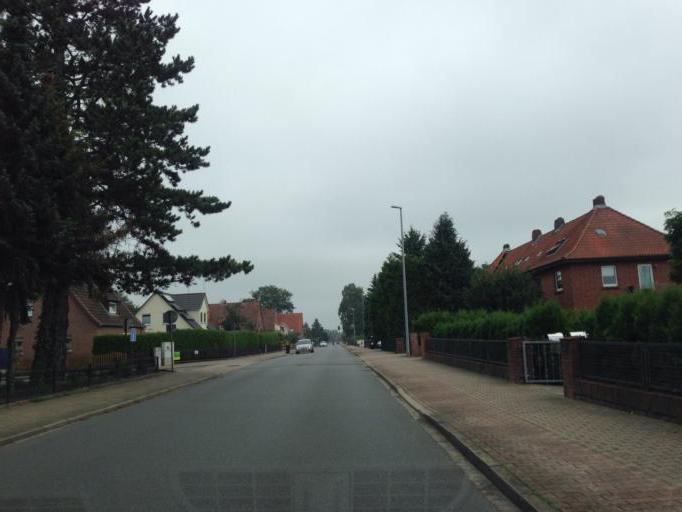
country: DE
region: Lower Saxony
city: Adendorf
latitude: 53.2851
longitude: 10.4293
